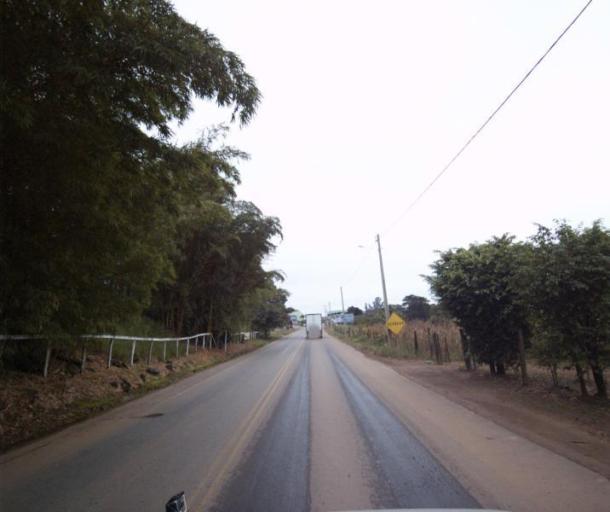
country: BR
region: Goias
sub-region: Pirenopolis
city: Pirenopolis
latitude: -15.9328
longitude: -48.8055
